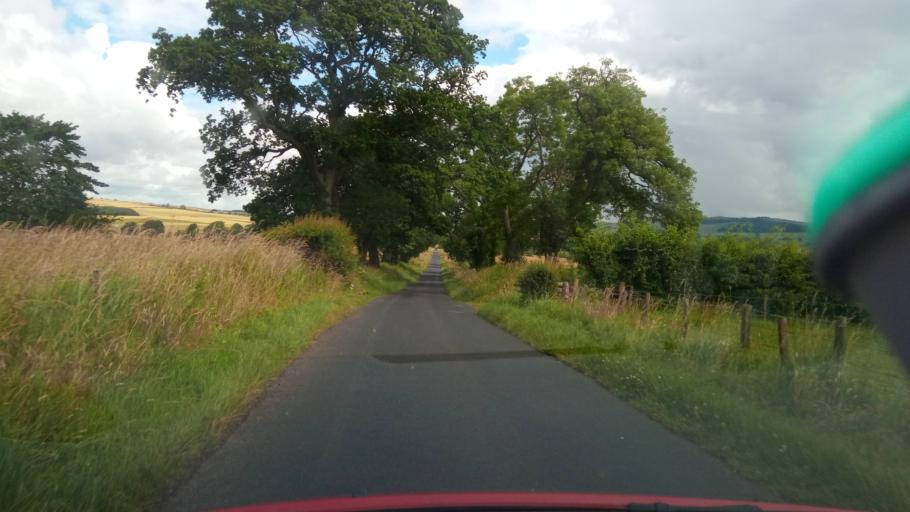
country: GB
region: Scotland
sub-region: The Scottish Borders
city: Kelso
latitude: 55.5162
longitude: -2.4128
